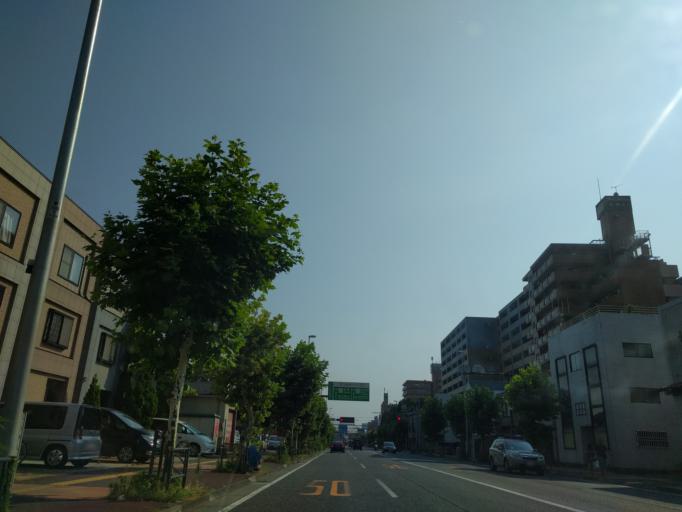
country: JP
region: Kanagawa
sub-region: Kawasaki-shi
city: Kawasaki
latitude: 35.4977
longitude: 139.6719
